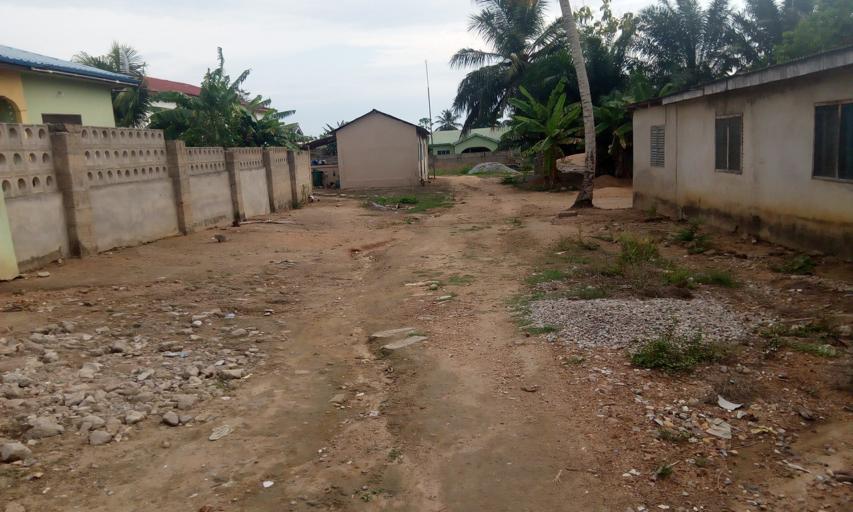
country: GH
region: Central
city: Winneba
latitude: 5.3587
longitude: -0.6244
